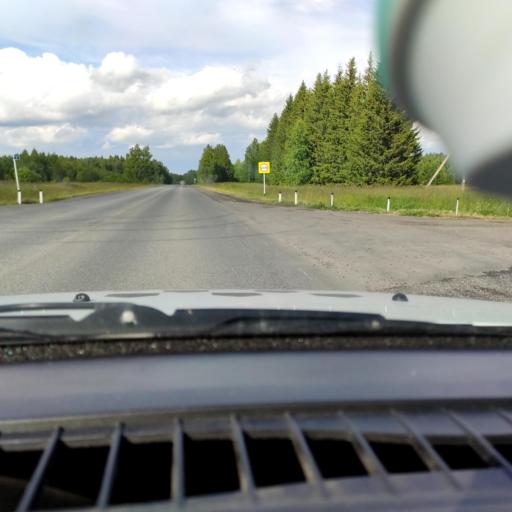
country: RU
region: Perm
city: Orda
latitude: 57.2443
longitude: 56.9904
